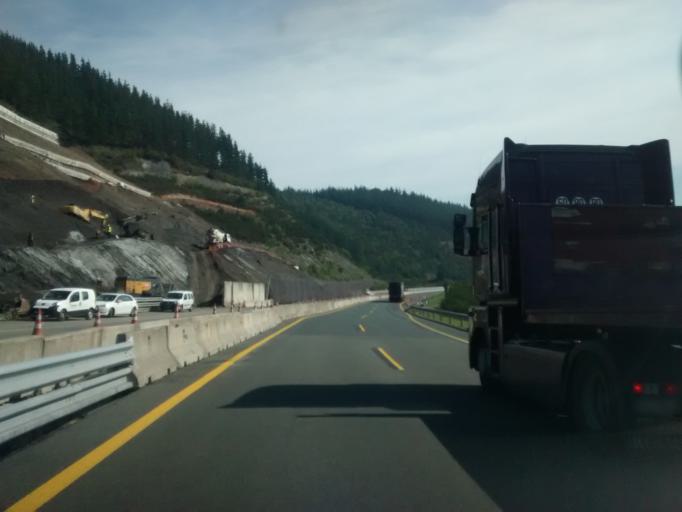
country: ES
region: Basque Country
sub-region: Provincia de Guipuzcoa
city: Eskoriatza
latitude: 43.0162
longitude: -2.5495
